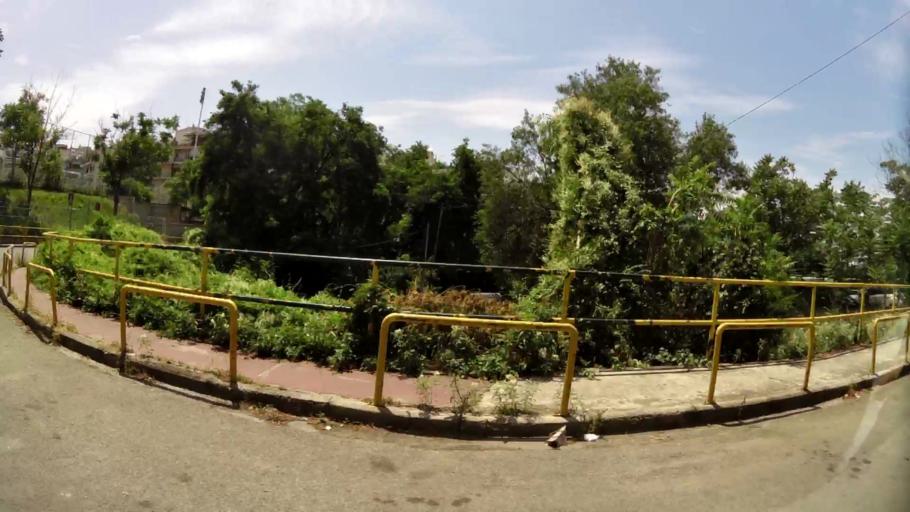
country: GR
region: Central Macedonia
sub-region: Nomos Thessalonikis
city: Triandria
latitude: 40.6212
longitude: 22.9735
